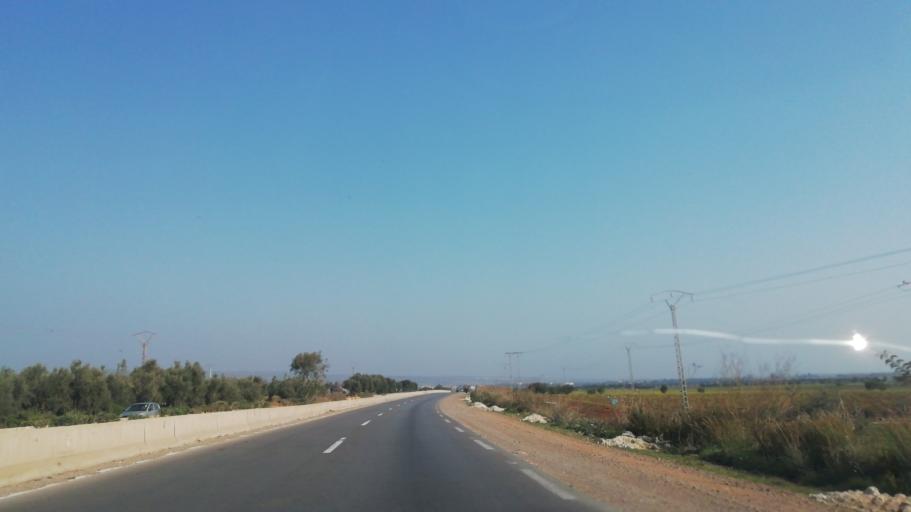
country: DZ
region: Oran
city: Bou Tlelis
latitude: 35.5602
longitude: -0.9306
